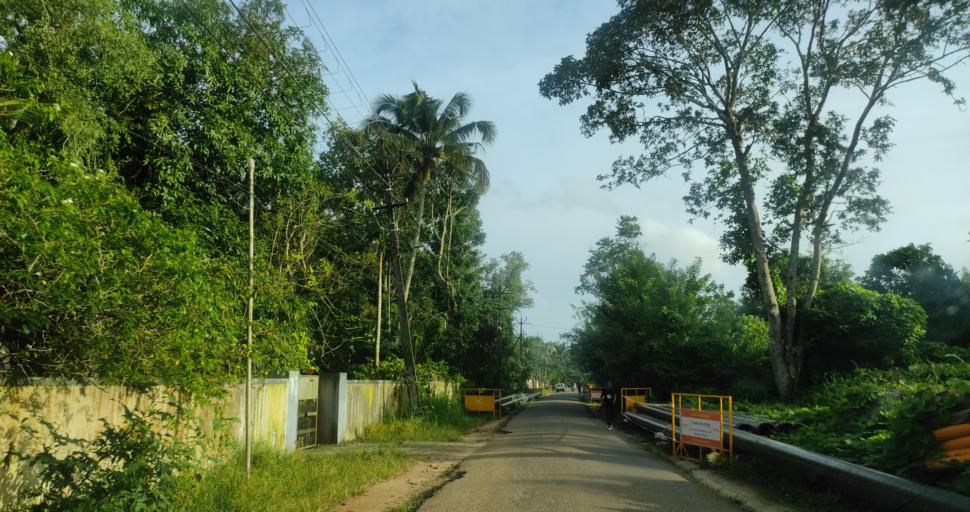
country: IN
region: Kerala
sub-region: Alappuzha
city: Shertallai
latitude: 9.6371
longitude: 76.3435
